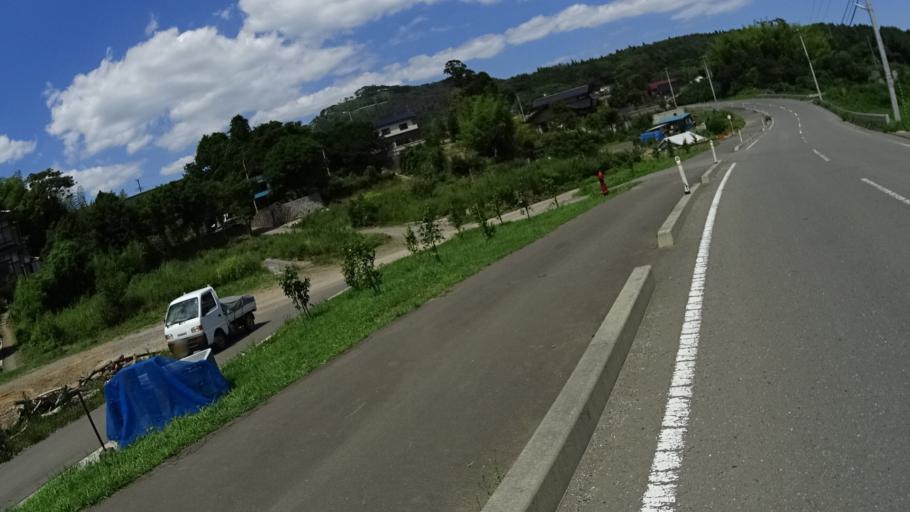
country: JP
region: Iwate
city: Ofunato
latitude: 38.8619
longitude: 141.6173
